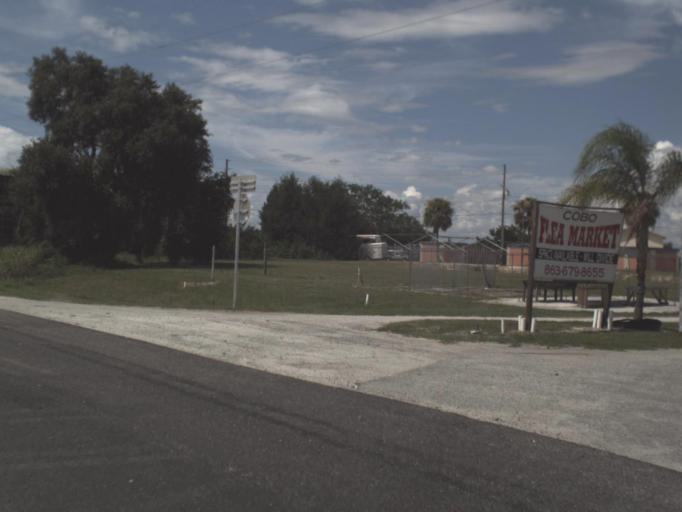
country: US
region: Florida
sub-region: Polk County
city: Lake Wales
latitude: 27.9032
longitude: -81.6098
